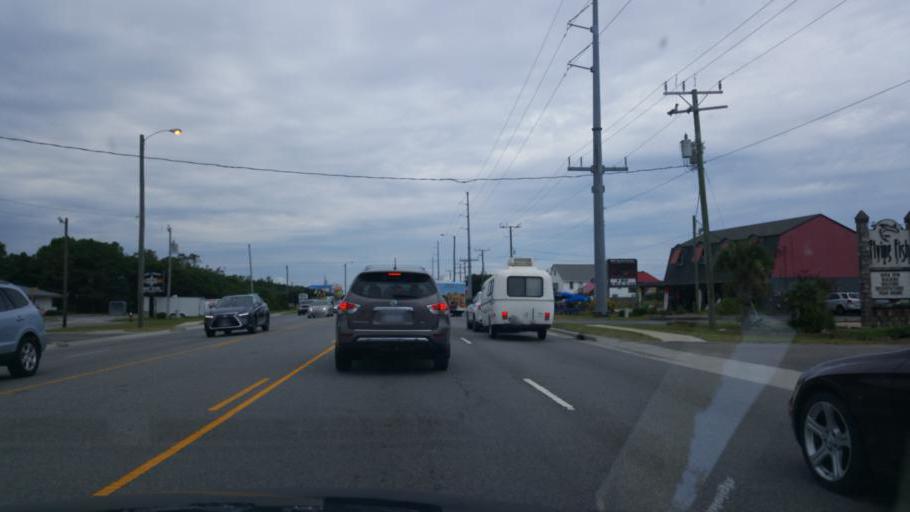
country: US
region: North Carolina
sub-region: Dare County
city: Kill Devil Hills
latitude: 35.9946
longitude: -75.6495
